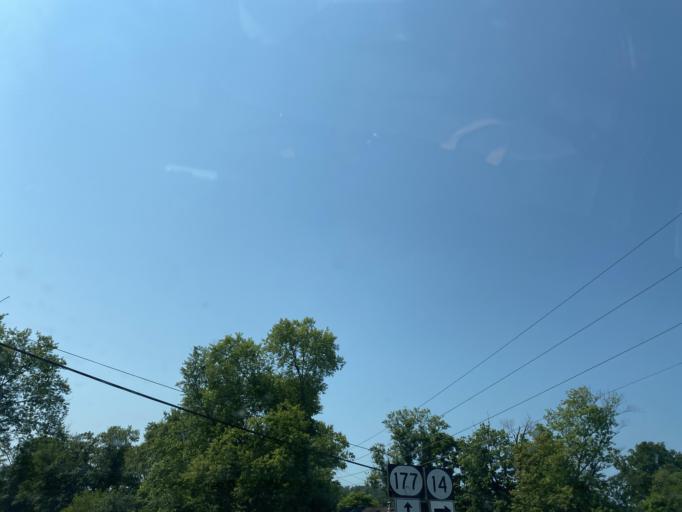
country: US
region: Kentucky
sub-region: Campbell County
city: Claryville
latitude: 38.8309
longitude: -84.4579
